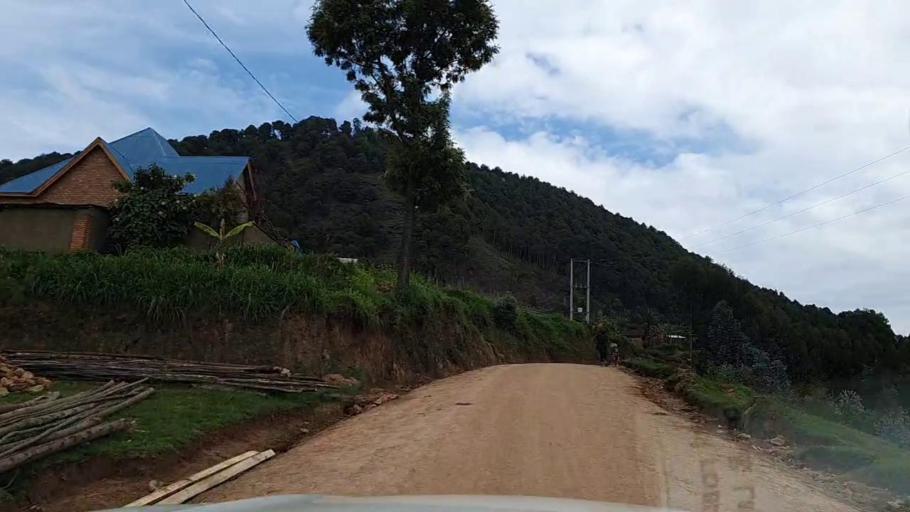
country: RW
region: Southern Province
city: Nzega
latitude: -2.3967
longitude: 29.4531
